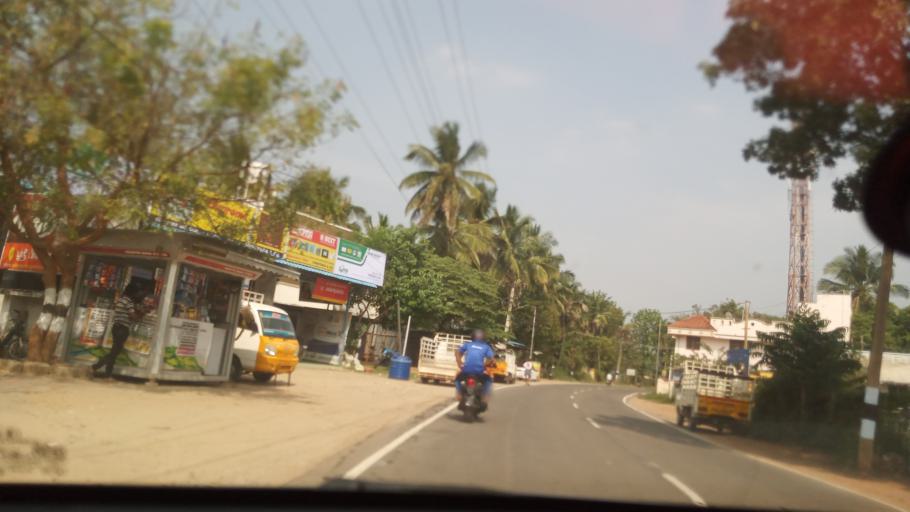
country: IN
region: Tamil Nadu
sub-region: Coimbatore
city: Perur
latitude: 10.9969
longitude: 76.8478
